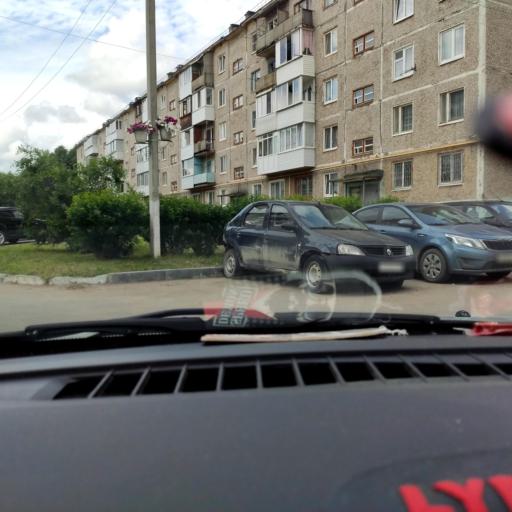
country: RU
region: Perm
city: Zvezdnyy
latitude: 57.7377
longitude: 56.3119
